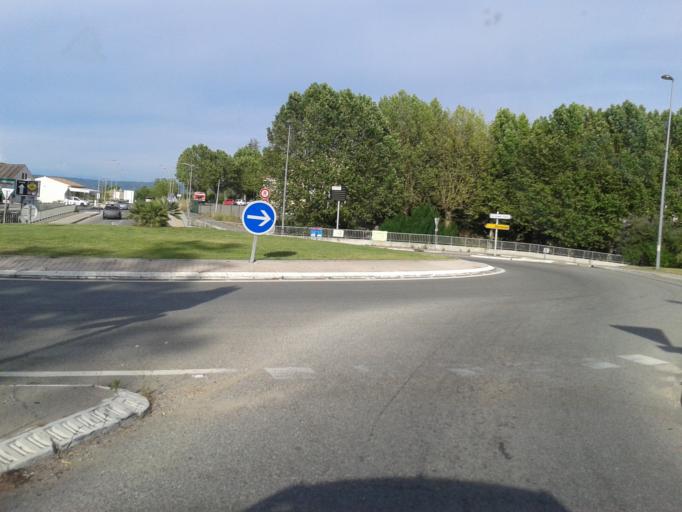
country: FR
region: Provence-Alpes-Cote d'Azur
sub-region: Departement des Bouches-du-Rhone
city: Meyrargues
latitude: 43.6404
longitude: 5.5252
